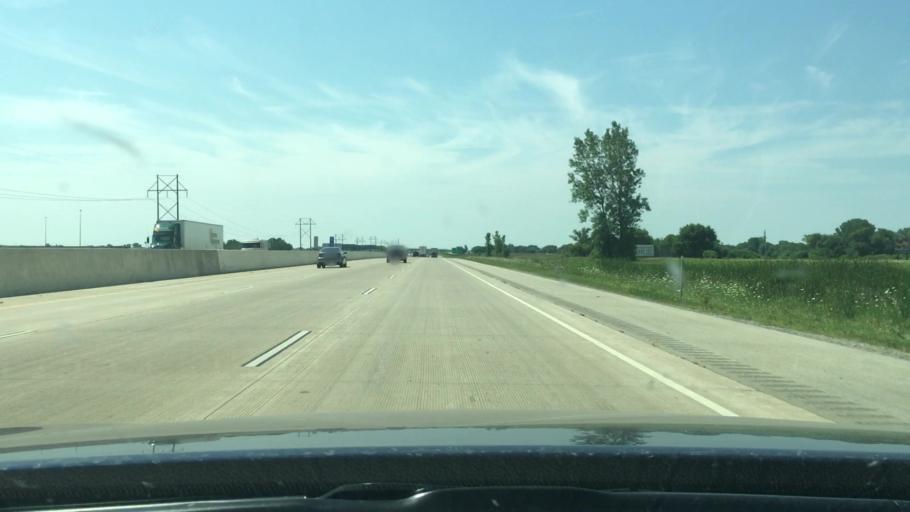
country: US
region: Wisconsin
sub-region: Winnebago County
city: Oshkosh
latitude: 44.0820
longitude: -88.5614
